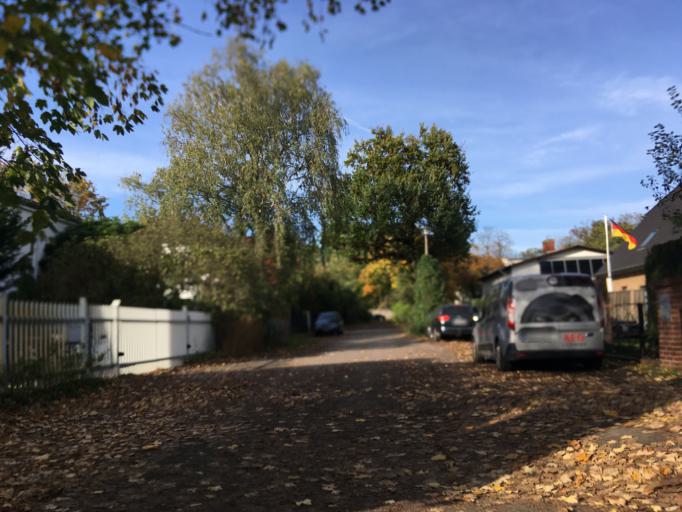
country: DE
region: Berlin
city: Niederschonhausen
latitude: 52.5897
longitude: 13.3998
